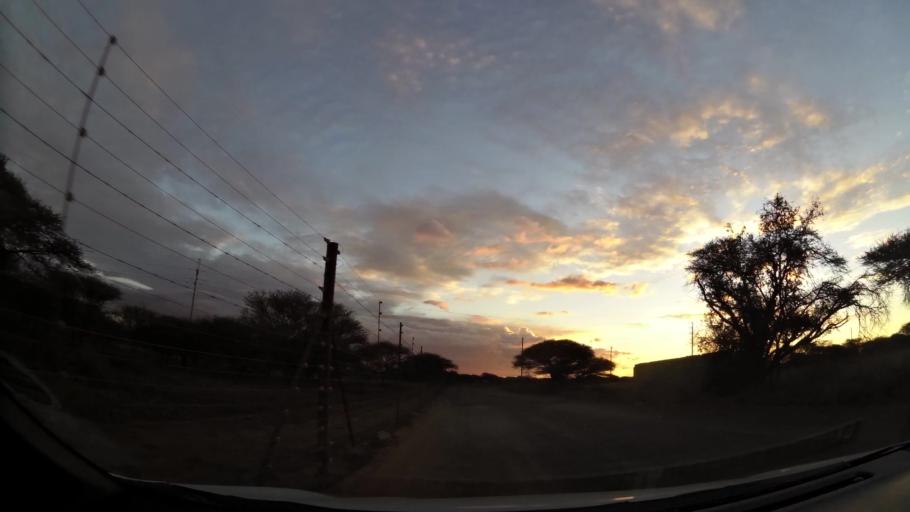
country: ZA
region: Limpopo
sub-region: Capricorn District Municipality
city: Polokwane
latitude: -23.7442
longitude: 29.4618
